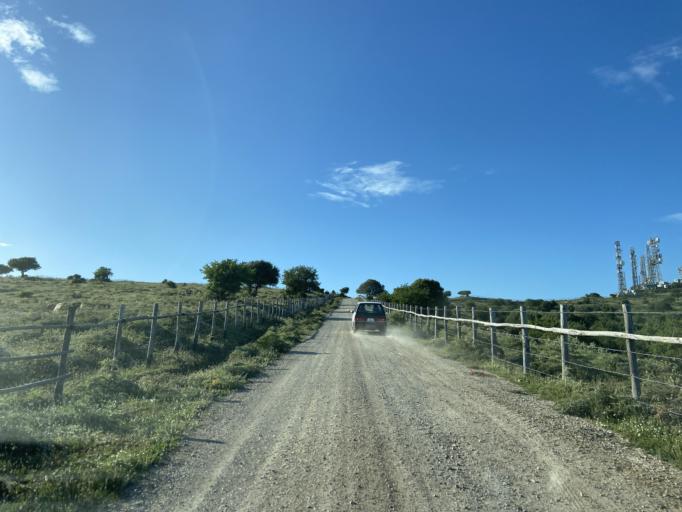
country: IT
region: Latium
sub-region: Citta metropolitana di Roma Capitale
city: Santa Marinella
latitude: 42.0861
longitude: 11.8523
